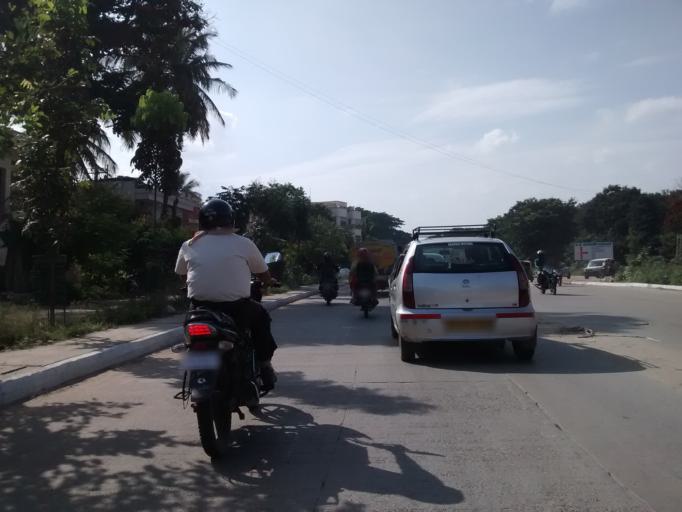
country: IN
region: Karnataka
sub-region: Bangalore Urban
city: Bangalore
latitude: 12.9764
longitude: 77.6551
